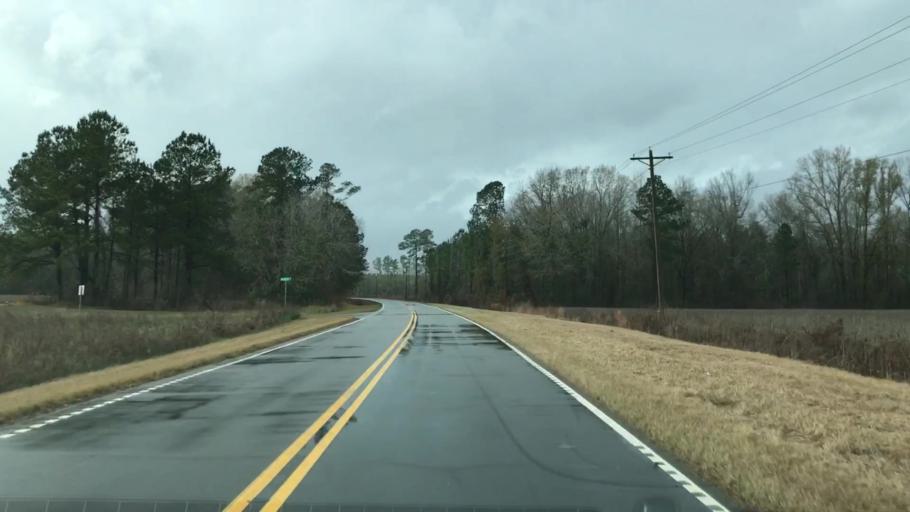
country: US
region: South Carolina
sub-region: Florence County
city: Johnsonville
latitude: 33.6755
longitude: -79.3336
